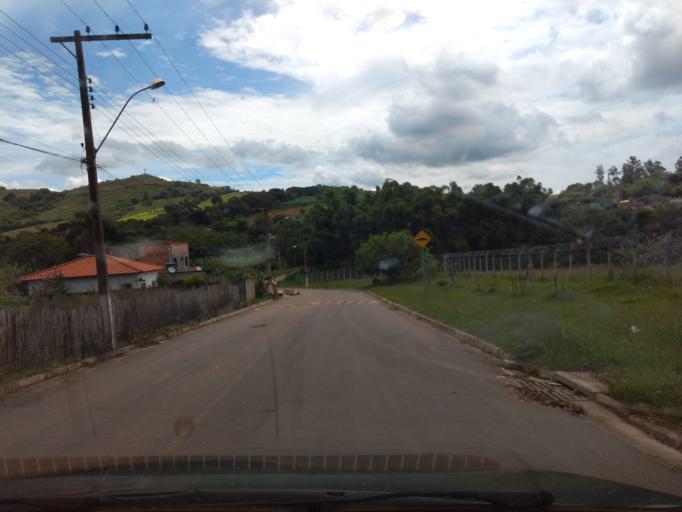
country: BR
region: Minas Gerais
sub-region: Lavras
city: Lavras
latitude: -21.5135
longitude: -44.9075
